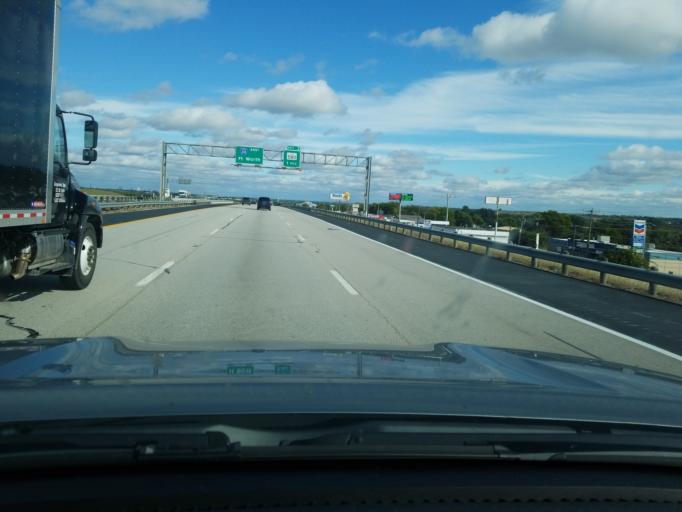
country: US
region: Texas
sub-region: Parker County
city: Aledo
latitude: 32.7208
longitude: -97.5353
